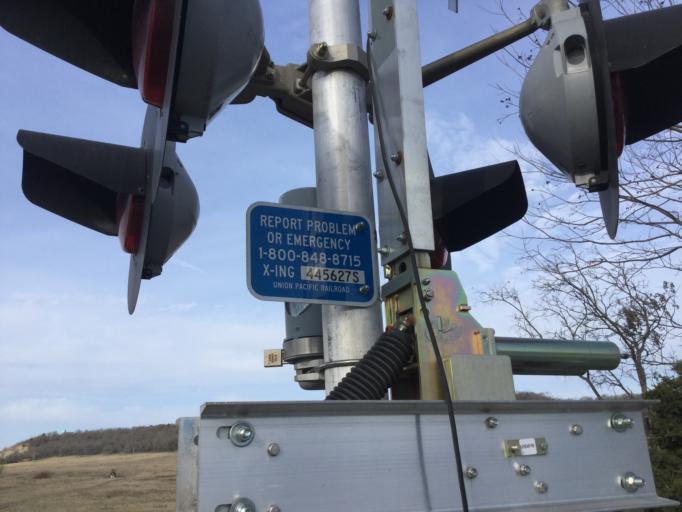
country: US
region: Kansas
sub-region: Wilson County
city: Neodesha
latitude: 37.3376
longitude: -95.7111
